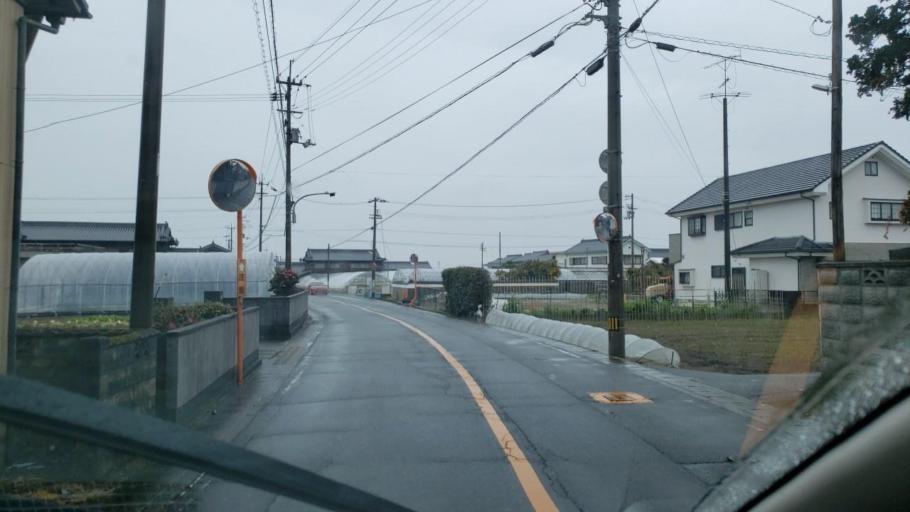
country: JP
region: Tokushima
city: Kamojimacho-jogejima
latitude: 34.0969
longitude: 134.3676
